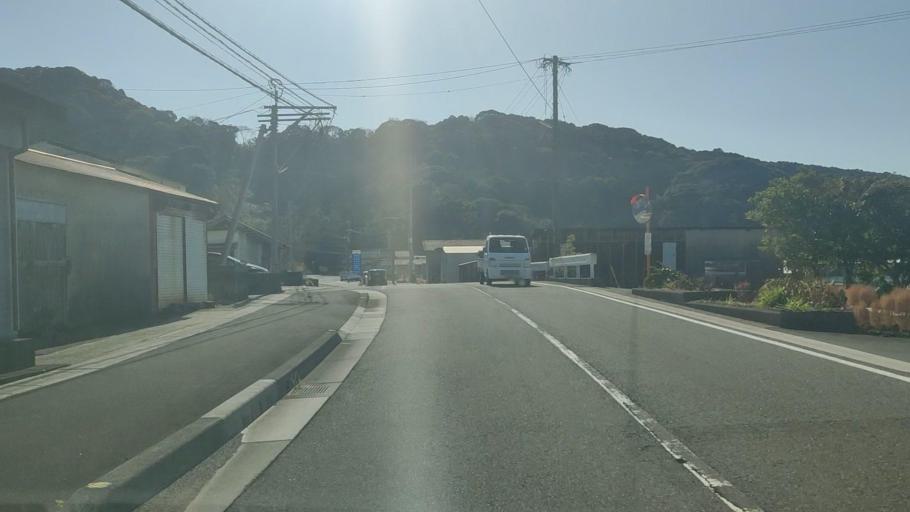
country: JP
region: Oita
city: Saiki
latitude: 32.8004
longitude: 131.9000
